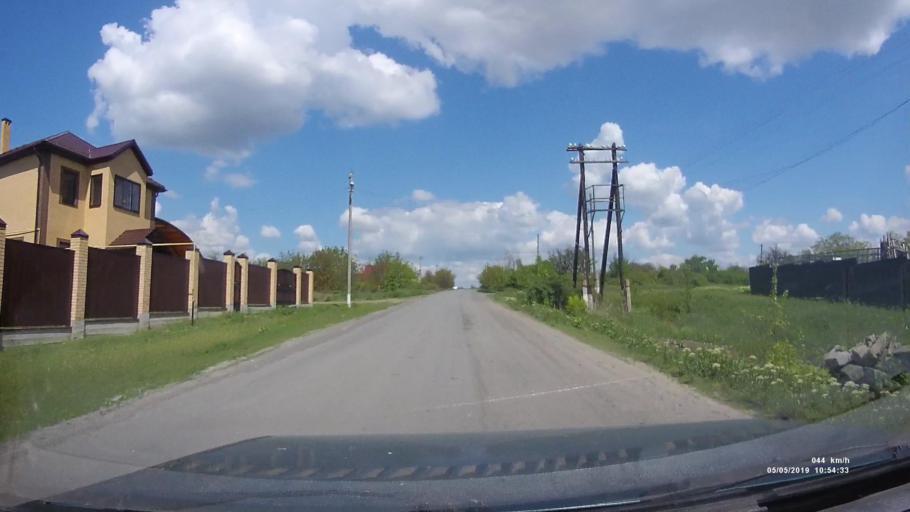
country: RU
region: Rostov
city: Ust'-Donetskiy
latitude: 47.6590
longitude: 40.8228
